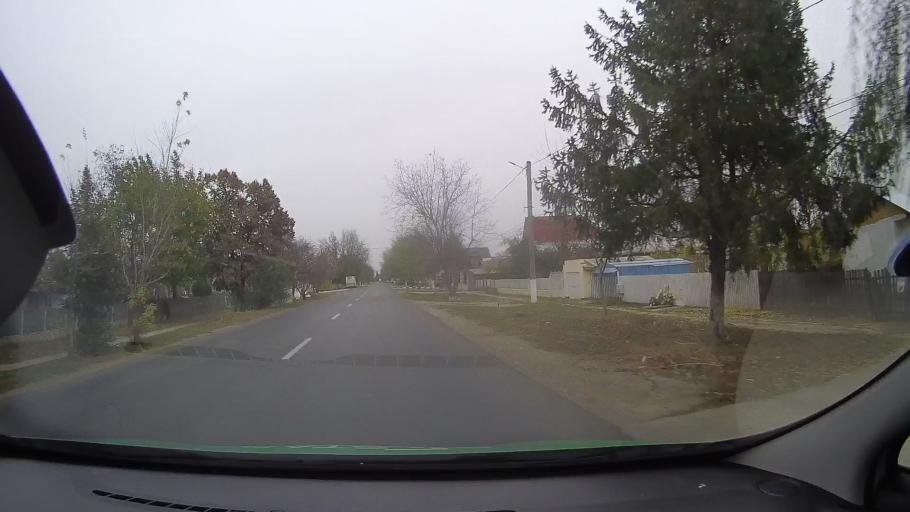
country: RO
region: Ialomita
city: Tandarei
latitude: 44.6479
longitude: 27.6554
